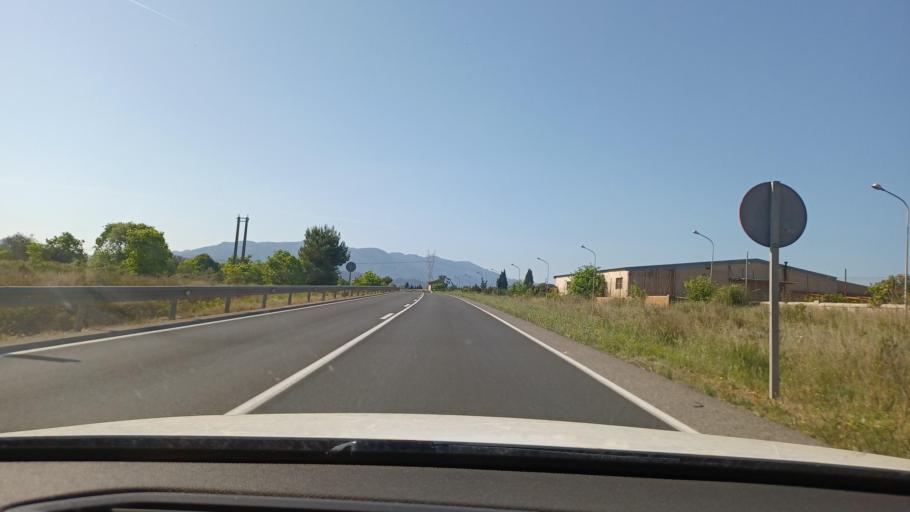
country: ES
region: Catalonia
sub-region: Provincia de Tarragona
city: Santa Barbara
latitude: 40.7150
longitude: 0.5061
